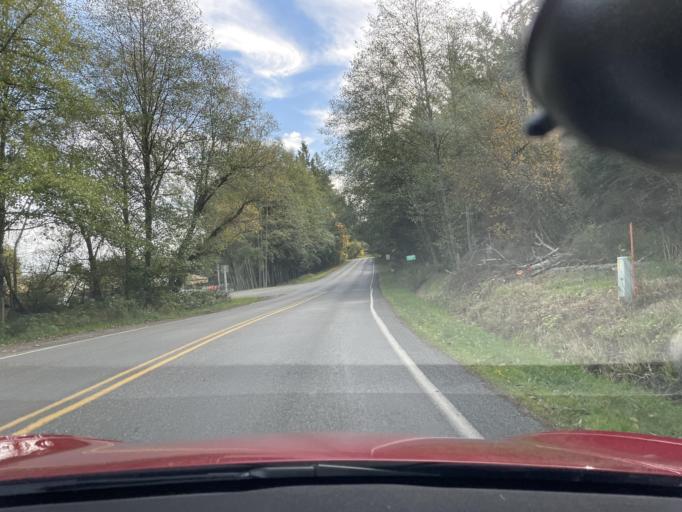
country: US
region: Washington
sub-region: San Juan County
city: Friday Harbor
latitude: 48.5396
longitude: -123.0342
